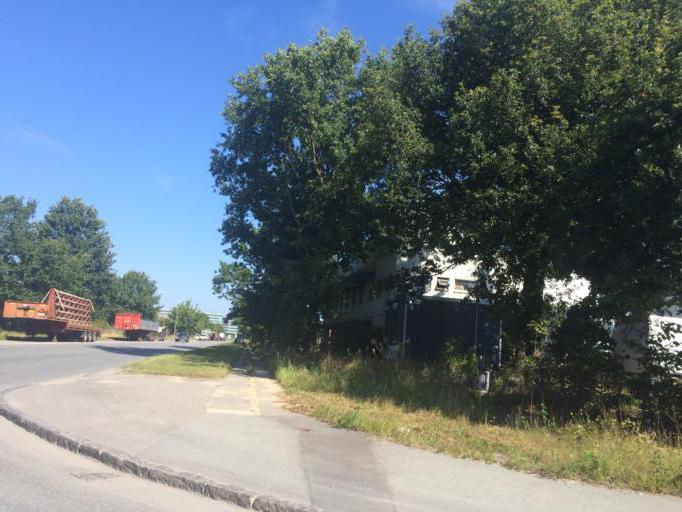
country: DK
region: Capital Region
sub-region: Hvidovre Kommune
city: Hvidovre
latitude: 55.6090
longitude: 12.4745
